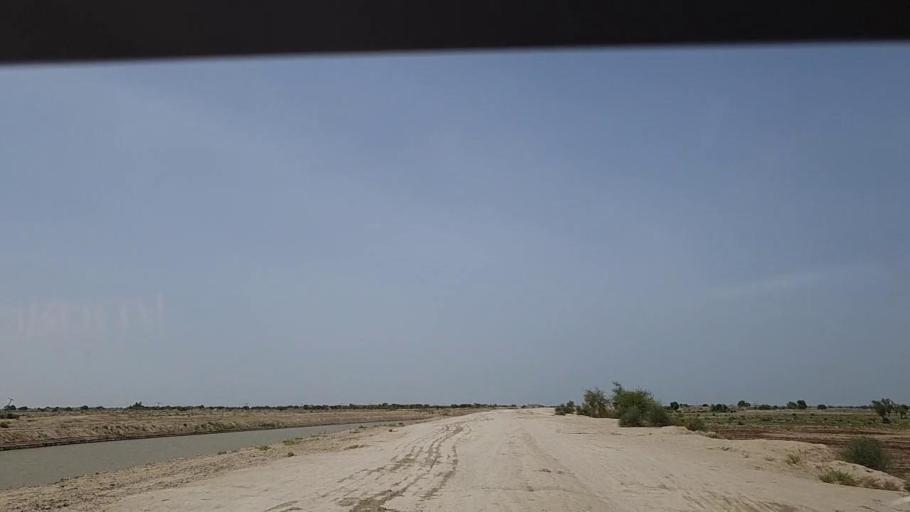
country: PK
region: Sindh
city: Johi
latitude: 26.7327
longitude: 67.6830
